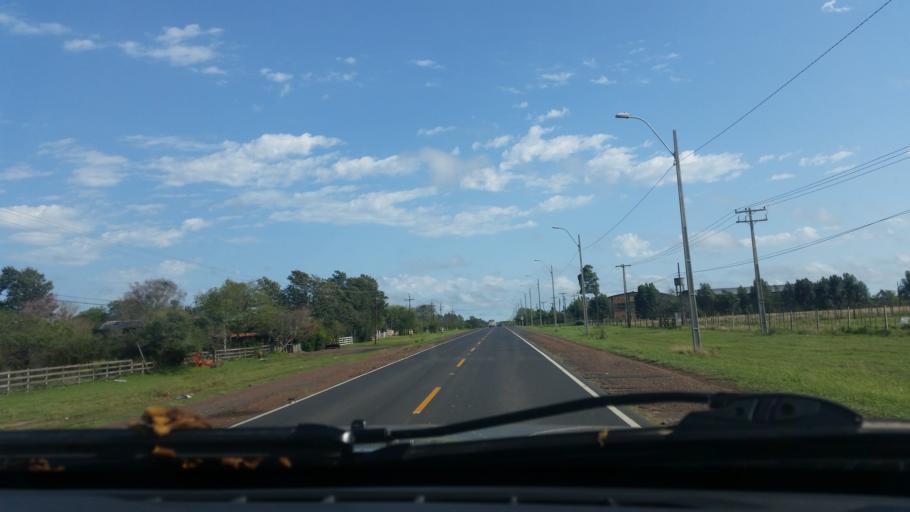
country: PY
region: Presidente Hayes
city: Villa Hayes
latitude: -25.0529
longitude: -57.5387
